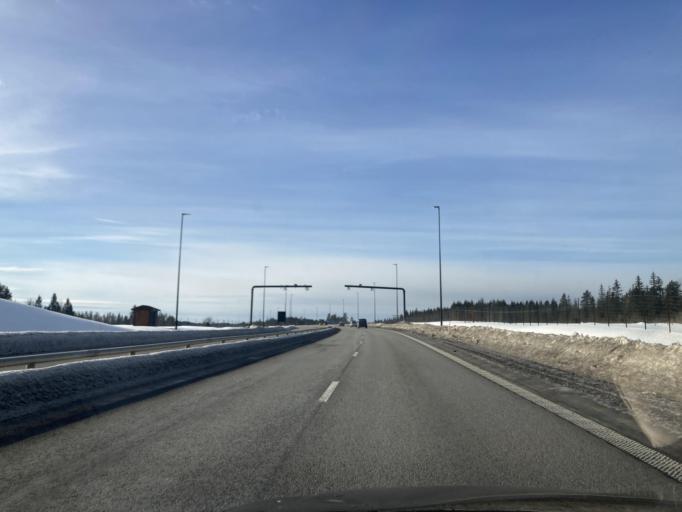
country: NO
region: Hedmark
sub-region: Elverum
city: Elverum
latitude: 60.8781
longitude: 11.4562
